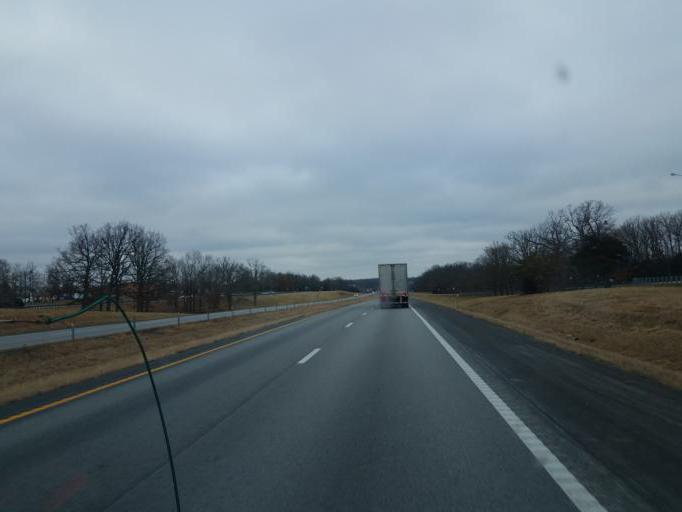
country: US
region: Missouri
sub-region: Webster County
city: Marshfield
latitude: 37.4751
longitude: -92.8567
